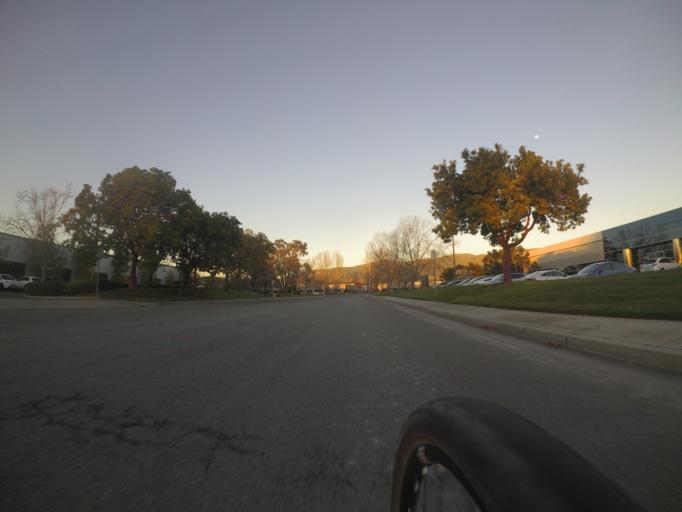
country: US
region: California
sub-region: Santa Clara County
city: Milpitas
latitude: 37.4717
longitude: -121.9388
